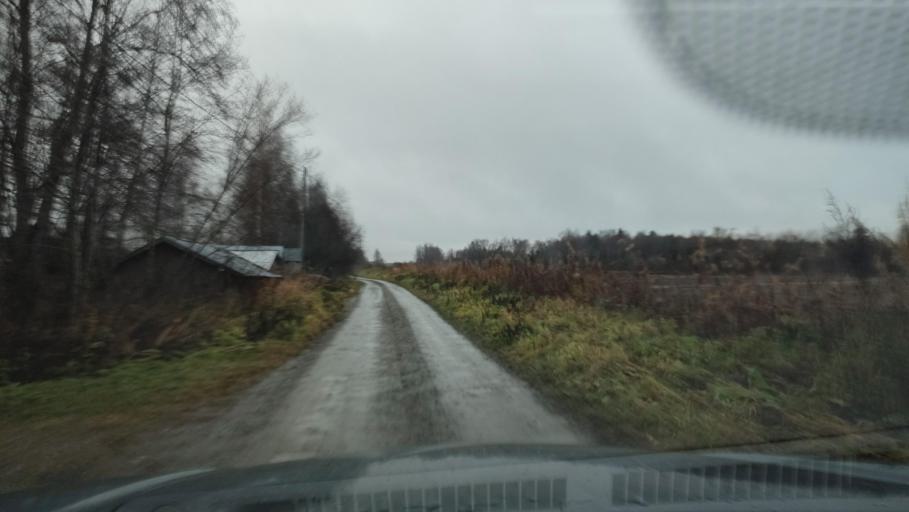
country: FI
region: Ostrobothnia
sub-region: Sydosterbotten
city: Kristinestad
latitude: 62.2291
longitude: 21.4478
